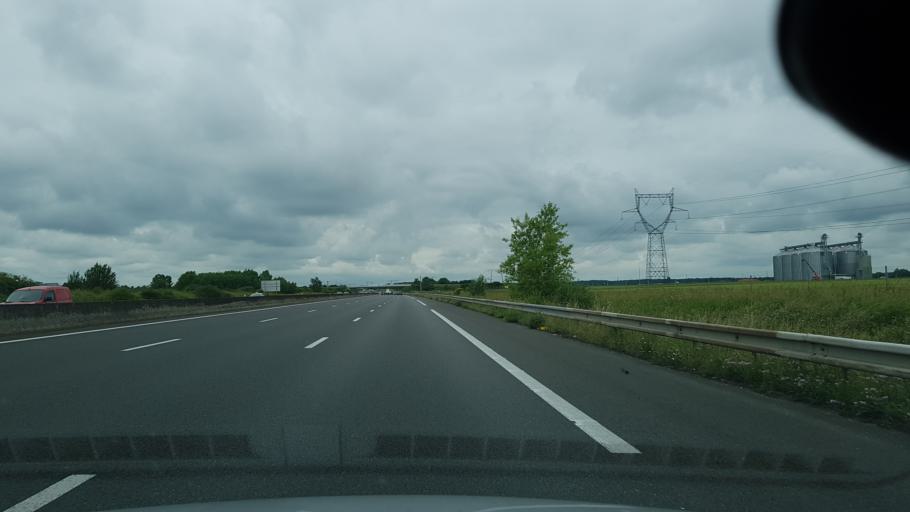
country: FR
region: Centre
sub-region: Departement du Loir-et-Cher
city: Herbault
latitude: 47.6146
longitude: 1.1548
